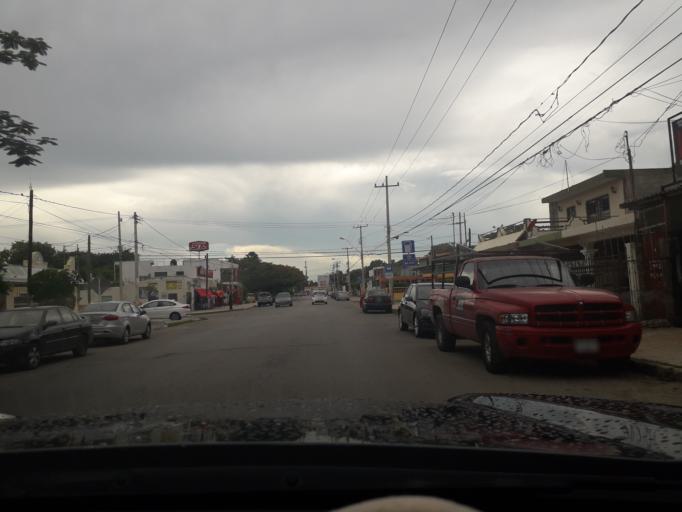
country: MX
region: Yucatan
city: Merida
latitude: 20.9543
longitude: -89.6489
